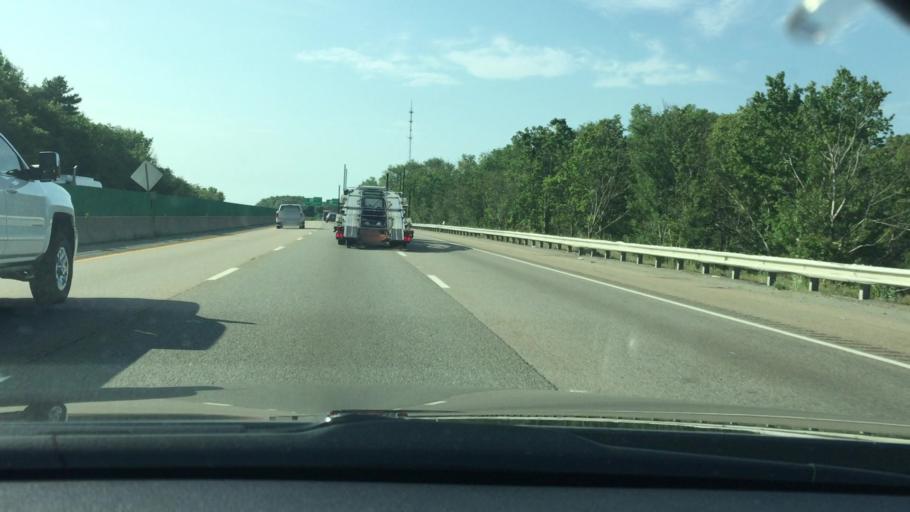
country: US
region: Massachusetts
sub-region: Plymouth County
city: West Bridgewater
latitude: 42.0209
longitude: -71.0477
